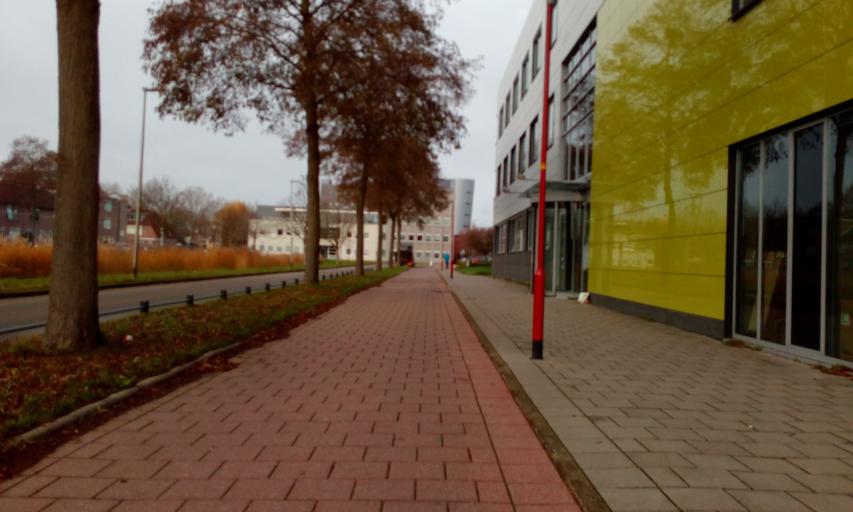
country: NL
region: South Holland
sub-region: Gemeente Zoetermeer
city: Zoetermeer
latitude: 52.0446
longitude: 4.4936
